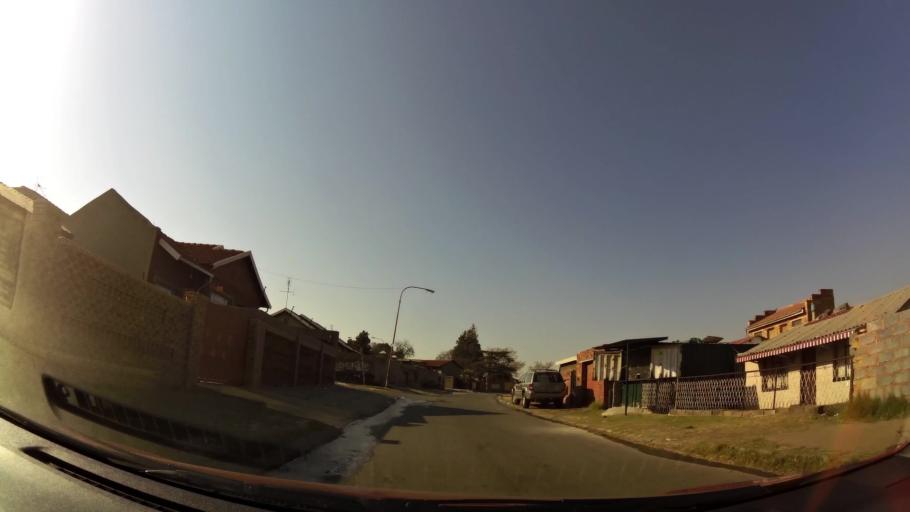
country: ZA
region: Gauteng
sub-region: City of Johannesburg Metropolitan Municipality
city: Soweto
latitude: -26.2521
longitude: 27.9487
